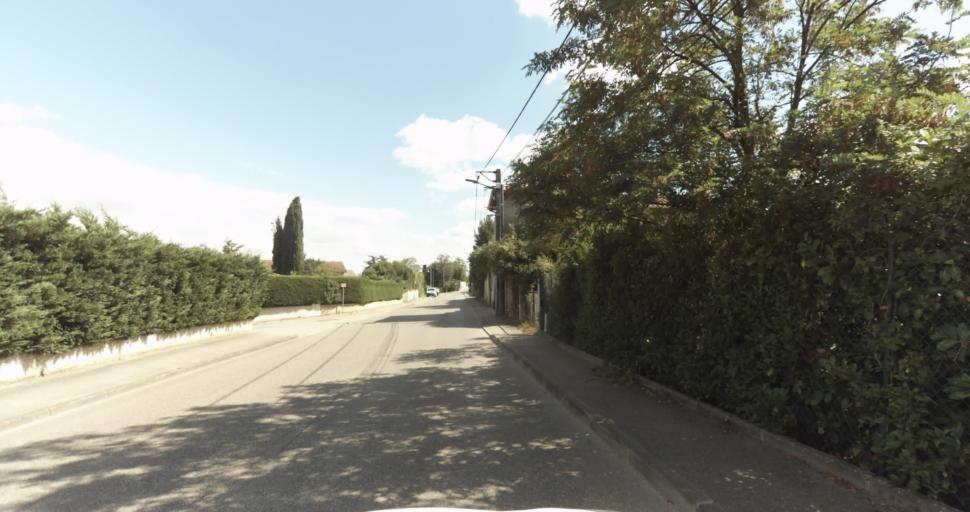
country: FR
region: Rhone-Alpes
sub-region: Departement du Rhone
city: Chaponost
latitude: 45.7025
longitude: 4.7487
